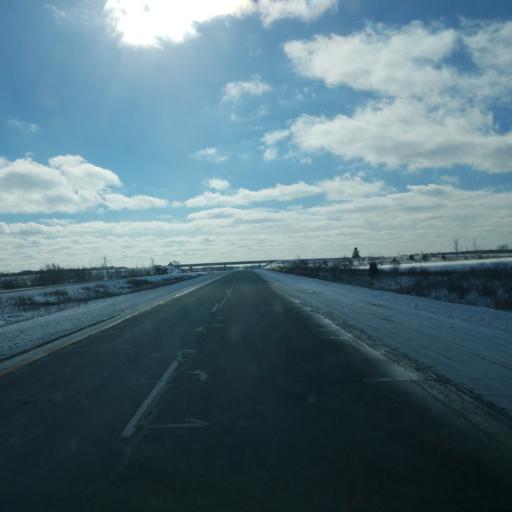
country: US
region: Michigan
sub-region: Clinton County
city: Saint Johns
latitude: 42.9912
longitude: -84.5191
